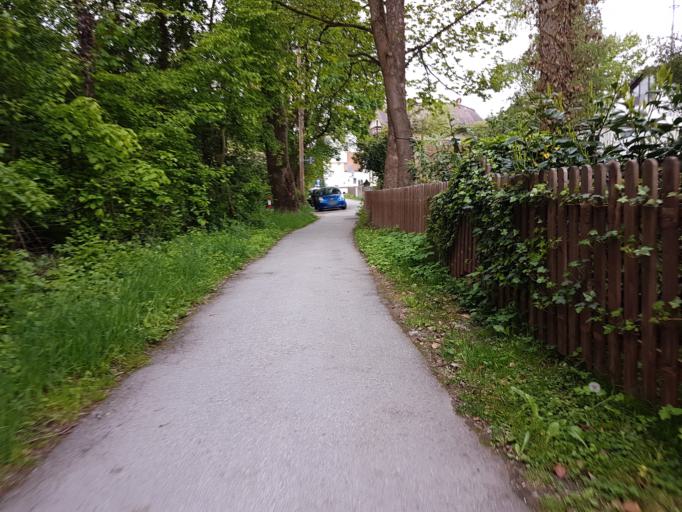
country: DE
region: Bavaria
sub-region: Upper Bavaria
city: Pasing
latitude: 48.1699
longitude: 11.4589
